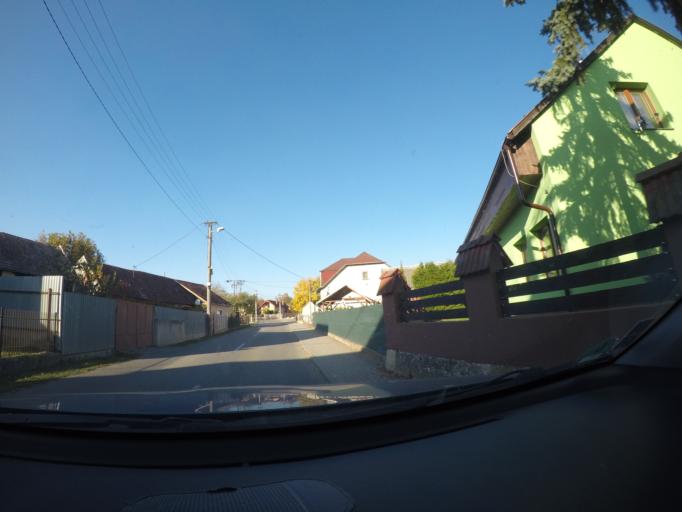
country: SK
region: Nitriansky
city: Nemsova
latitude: 48.9615
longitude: 18.1056
